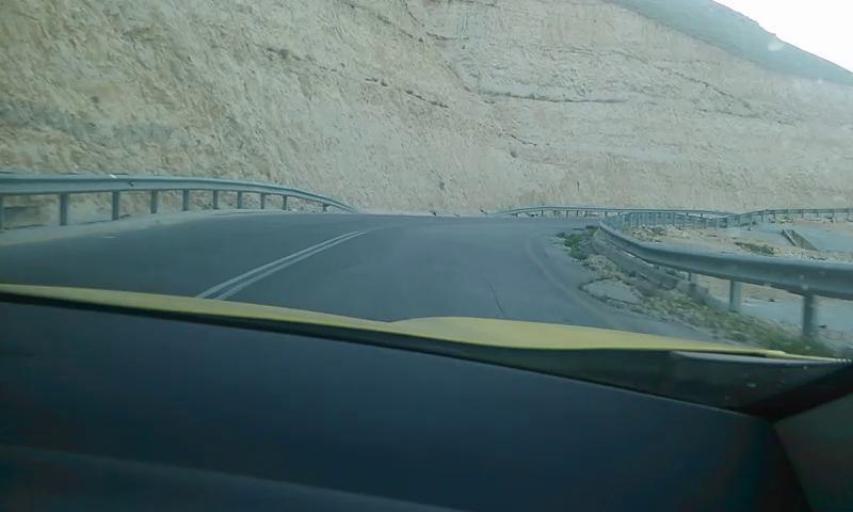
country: PS
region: West Bank
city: An Nuway`imah
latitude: 31.9099
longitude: 35.3727
